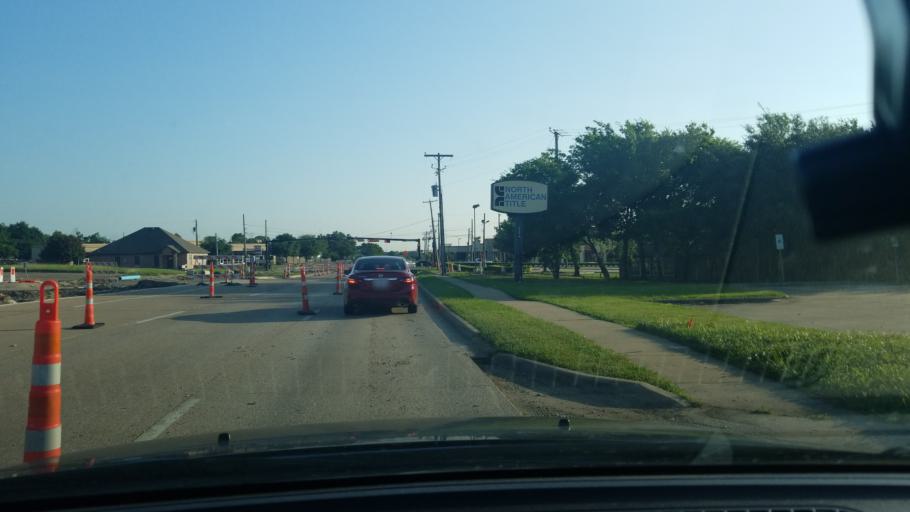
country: US
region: Texas
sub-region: Dallas County
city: Mesquite
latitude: 32.7975
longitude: -96.6340
